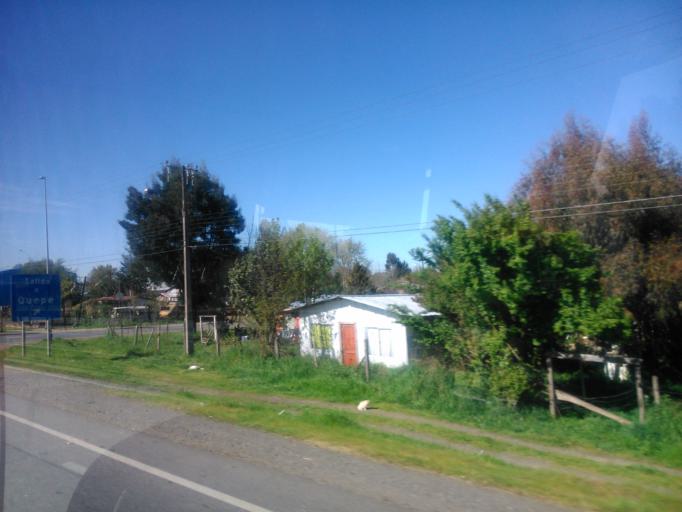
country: CL
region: Araucania
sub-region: Provincia de Cautin
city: Freire
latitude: -38.8714
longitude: -72.6173
